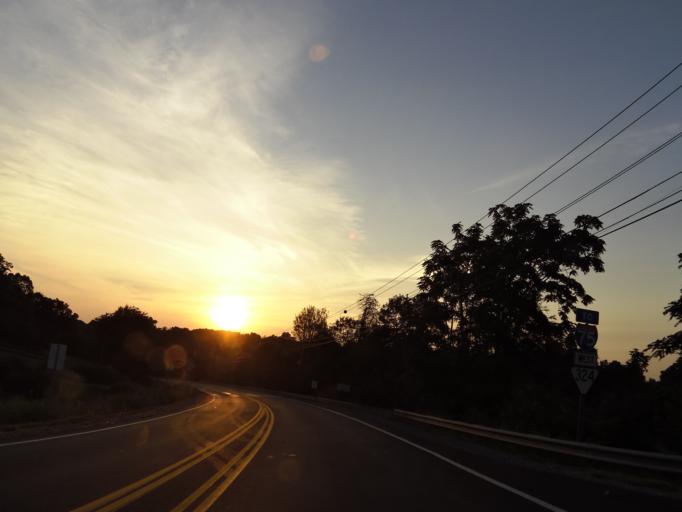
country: US
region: Tennessee
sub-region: Loudon County
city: Loudon
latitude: 35.7713
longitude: -84.3126
